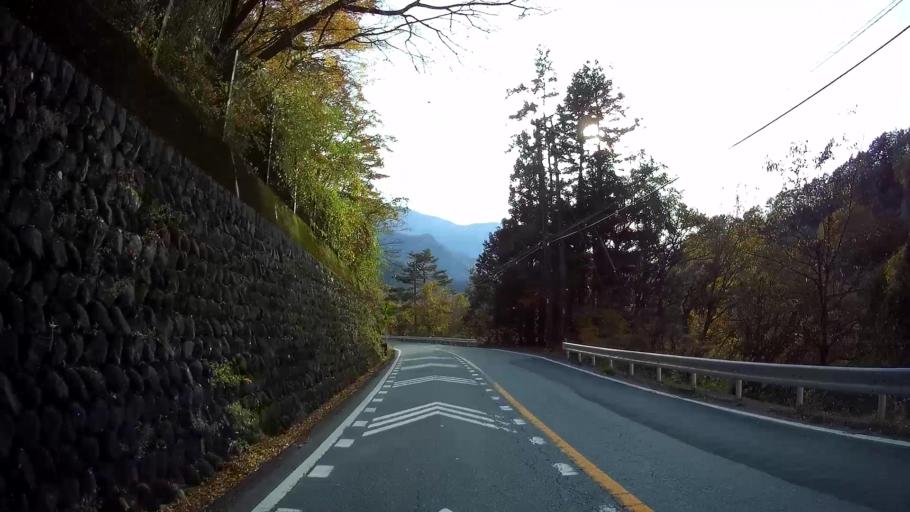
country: JP
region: Yamanashi
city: Fujikawaguchiko
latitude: 35.4790
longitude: 138.5561
